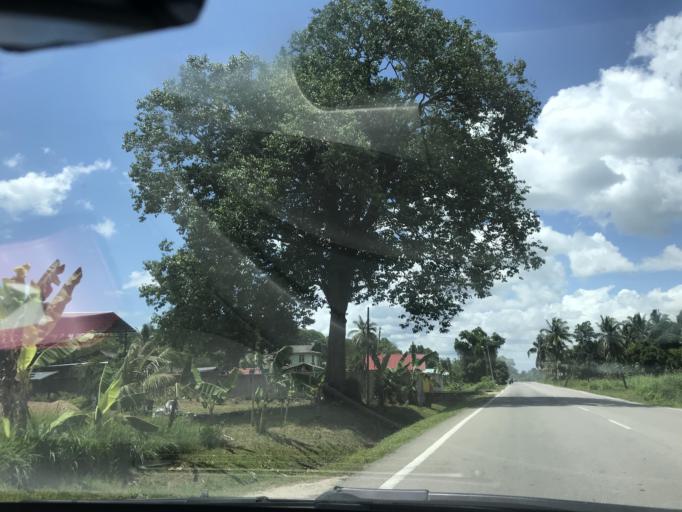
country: MY
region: Kelantan
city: Tumpat
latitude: 6.1964
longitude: 102.1352
